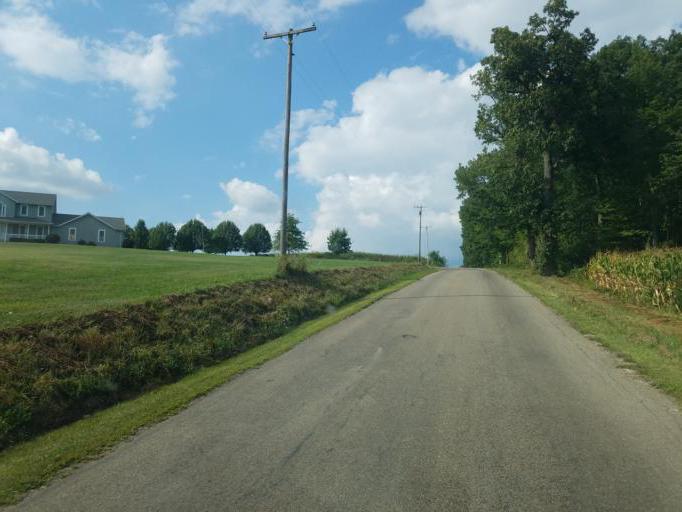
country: US
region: Ohio
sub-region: Knox County
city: Danville
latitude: 40.4941
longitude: -82.3345
